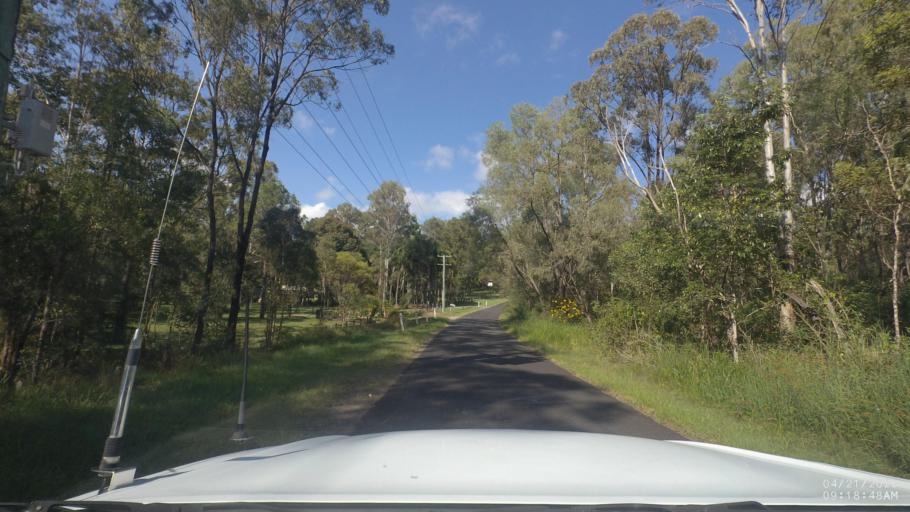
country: AU
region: Queensland
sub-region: Logan
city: Cedar Vale
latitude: -27.8461
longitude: 153.0827
